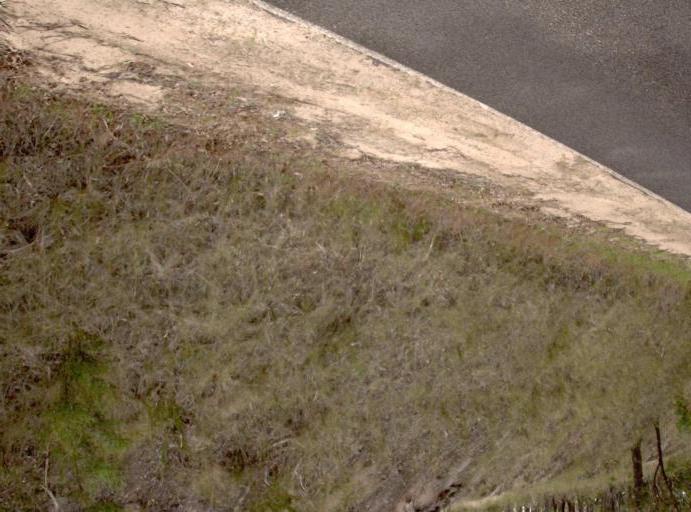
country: AU
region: Victoria
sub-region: Latrobe
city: Traralgon
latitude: -38.4074
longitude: 146.8237
